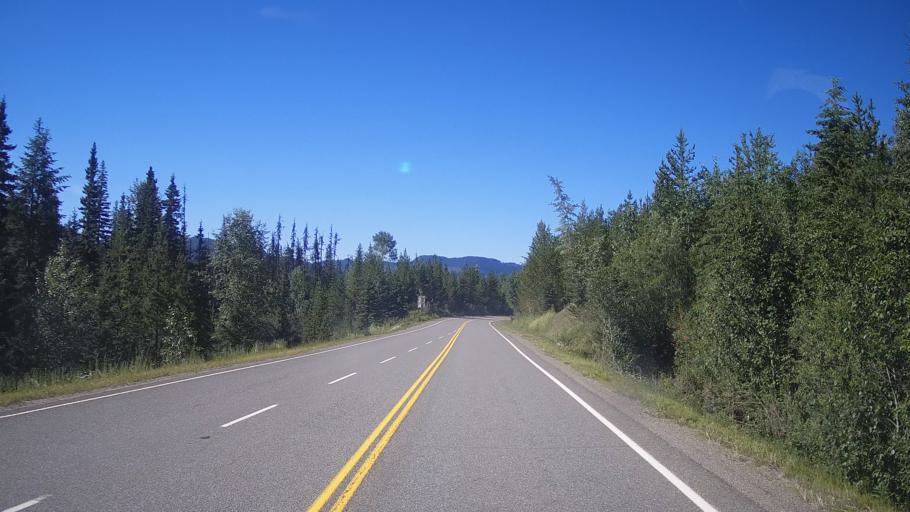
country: CA
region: British Columbia
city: Kamloops
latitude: 51.4880
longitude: -120.4617
